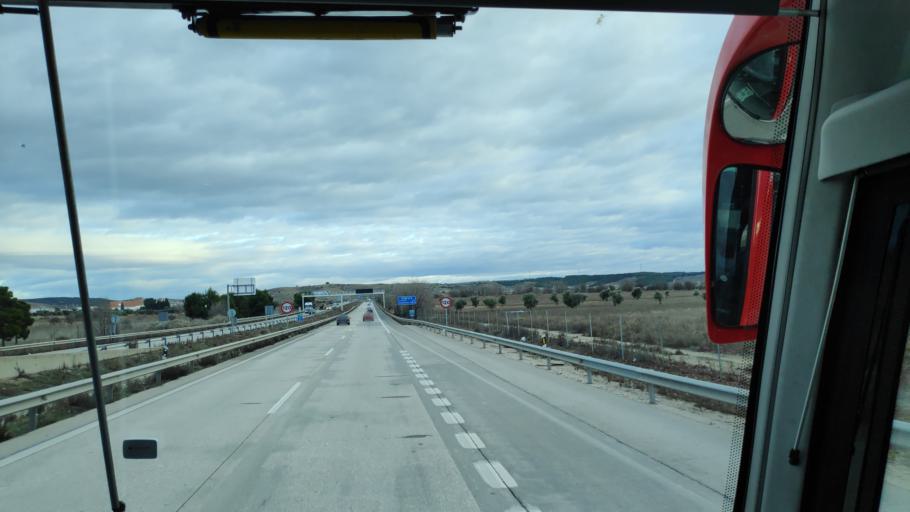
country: ES
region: Madrid
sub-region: Provincia de Madrid
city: Vaciamadrid
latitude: 40.3072
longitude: -3.4901
